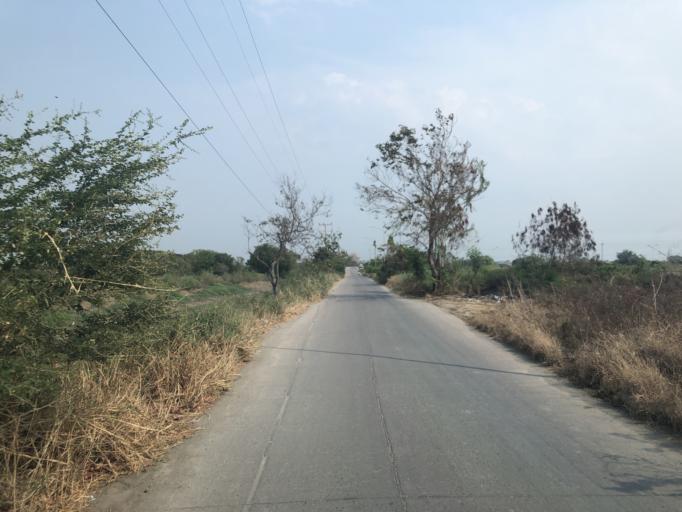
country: TH
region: Chachoengsao
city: Bang Pakong
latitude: 13.5125
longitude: 100.9239
